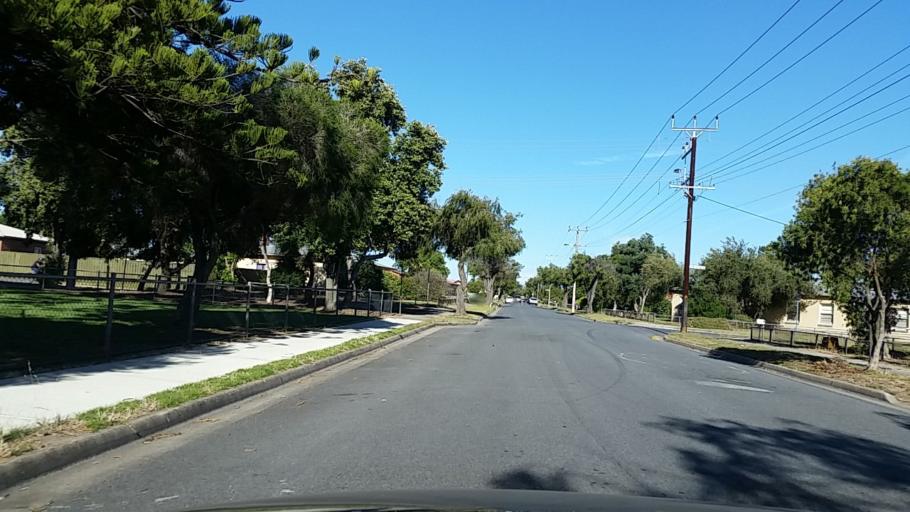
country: AU
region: South Australia
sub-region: Charles Sturt
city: Royal Park
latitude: -34.8813
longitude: 138.5072
